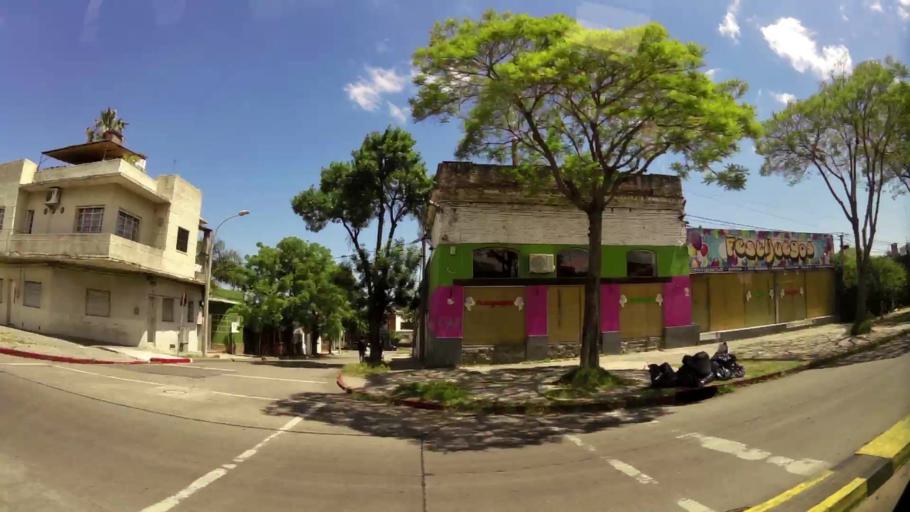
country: UY
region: Montevideo
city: Montevideo
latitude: -34.8627
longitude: -56.2183
